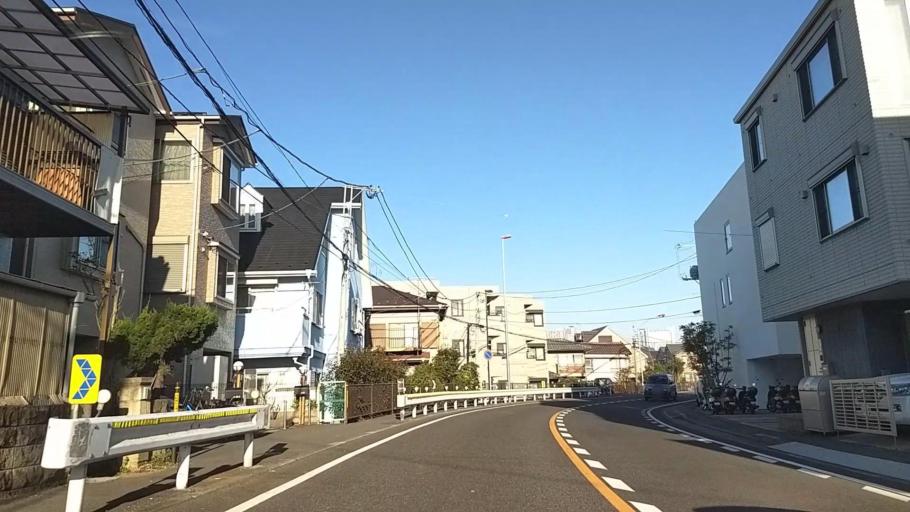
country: JP
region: Kanagawa
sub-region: Kawasaki-shi
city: Kawasaki
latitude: 35.5544
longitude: 139.6730
